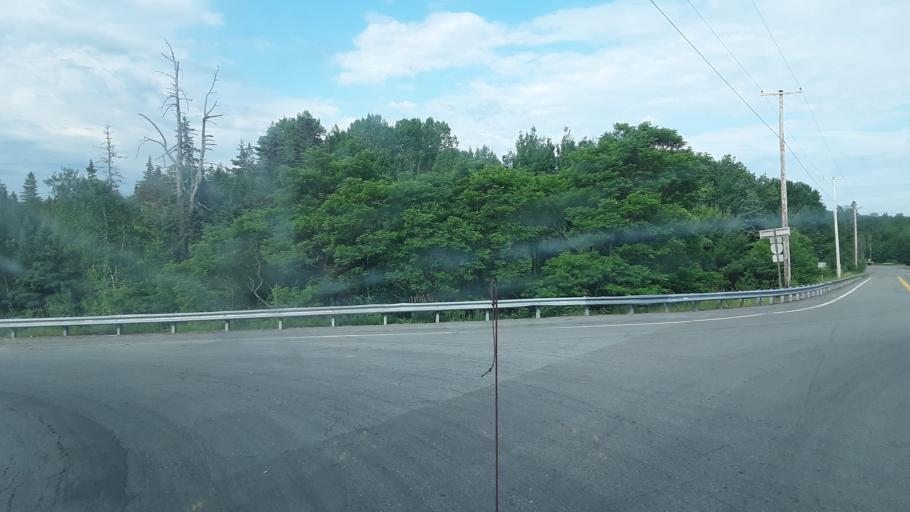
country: US
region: Maine
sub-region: Penobscot County
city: Lincoln
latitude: 45.3756
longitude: -68.6070
